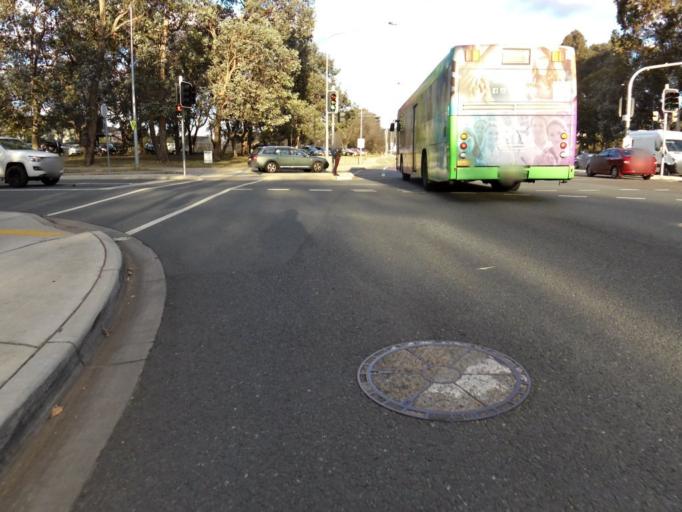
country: AU
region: Australian Capital Territory
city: Acton
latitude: -35.2732
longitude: 149.1219
